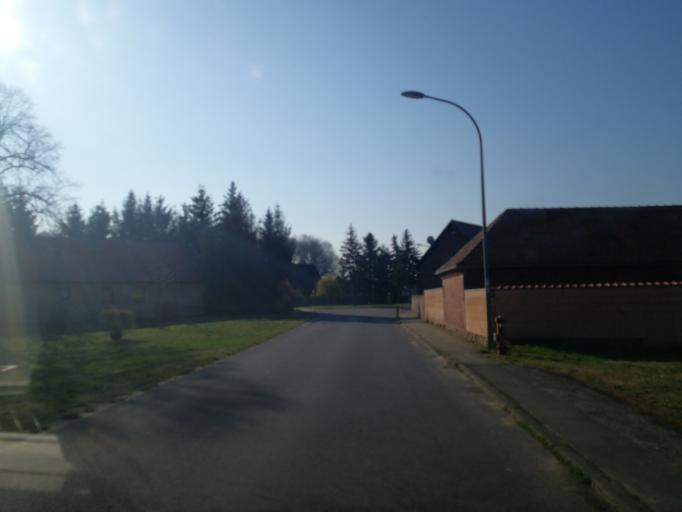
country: DE
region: Brandenburg
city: Drahnsdorf
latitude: 51.8712
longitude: 13.5923
